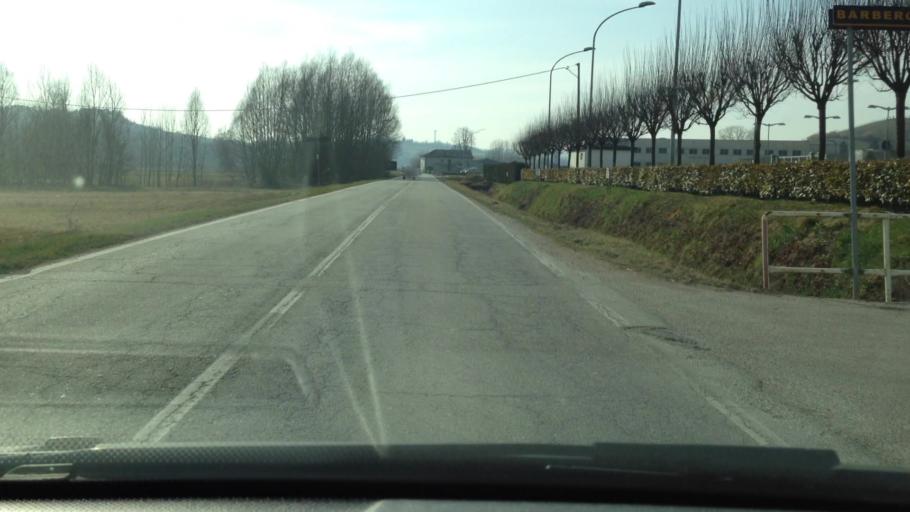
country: IT
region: Piedmont
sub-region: Provincia di Asti
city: Mombercelli
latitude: 44.8194
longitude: 8.2783
